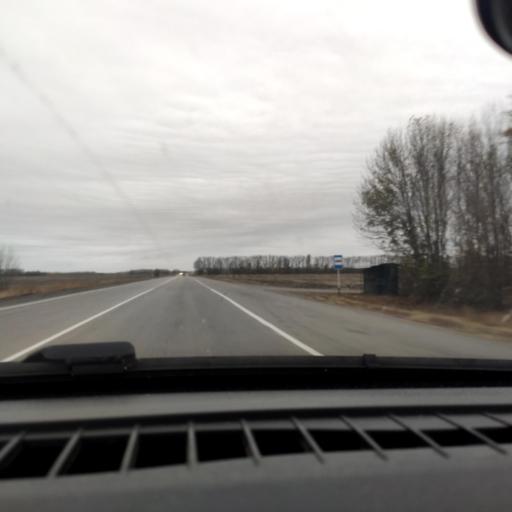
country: RU
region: Voronezj
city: Strelitsa
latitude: 51.5127
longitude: 38.9670
